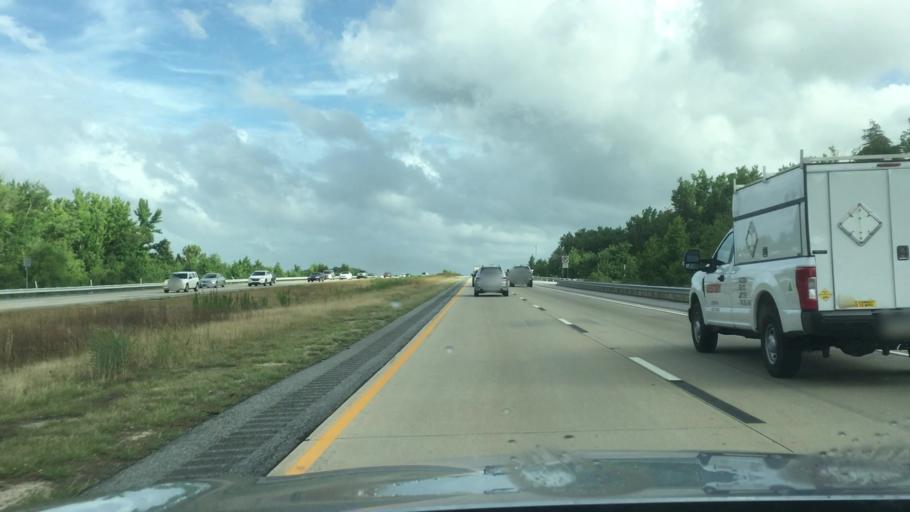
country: US
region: Delaware
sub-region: New Castle County
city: Townsend
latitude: 39.3894
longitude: -75.6663
